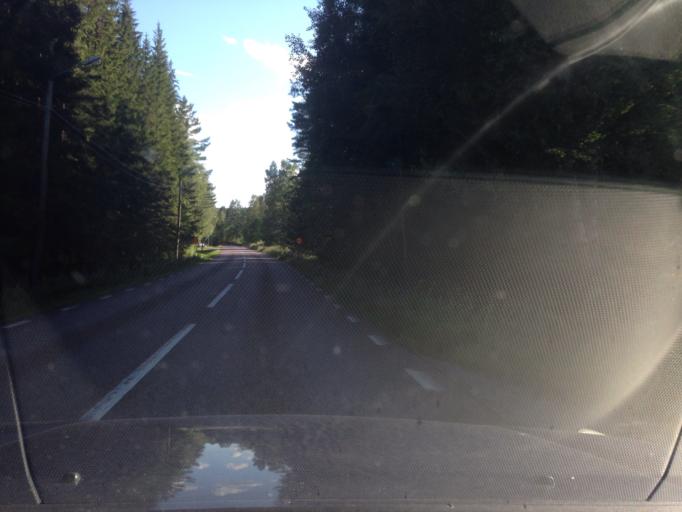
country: SE
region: Dalarna
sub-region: Ludvika Kommun
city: Grangesberg
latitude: 60.1652
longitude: 14.9738
